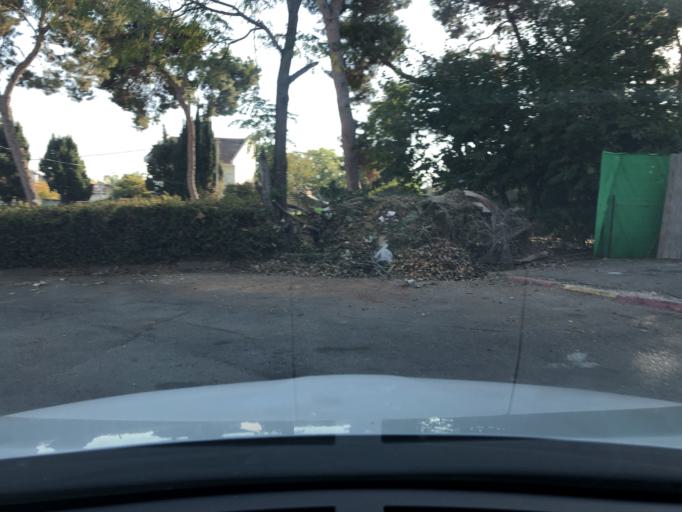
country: IL
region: Central District
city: Hod HaSharon
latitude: 32.1415
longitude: 34.9032
